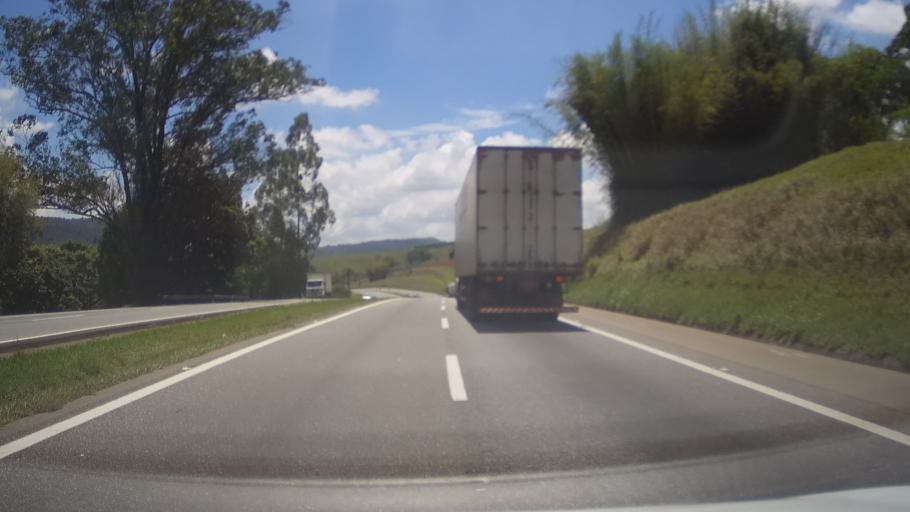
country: BR
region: Minas Gerais
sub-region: Campanha
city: Campanha
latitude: -21.8250
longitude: -45.4956
